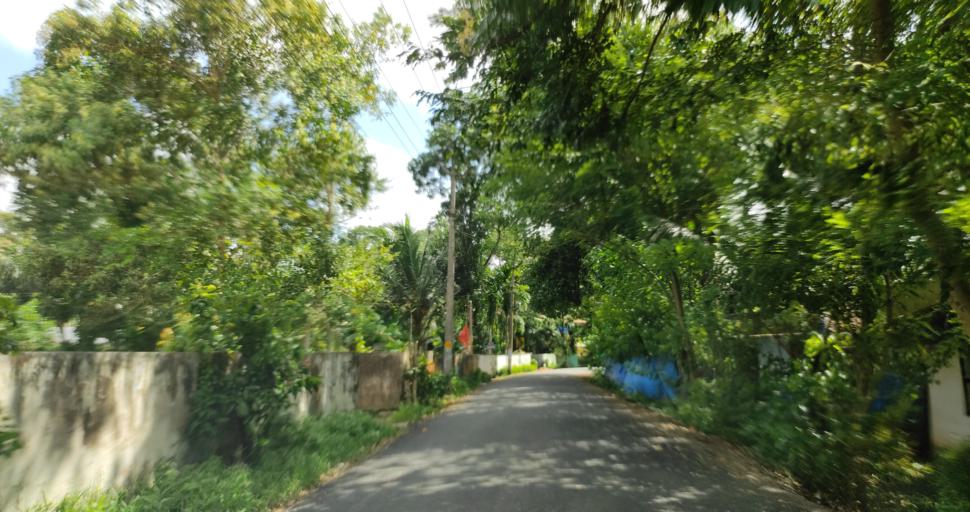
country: IN
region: Kerala
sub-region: Alappuzha
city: Shertallai
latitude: 9.6618
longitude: 76.3742
